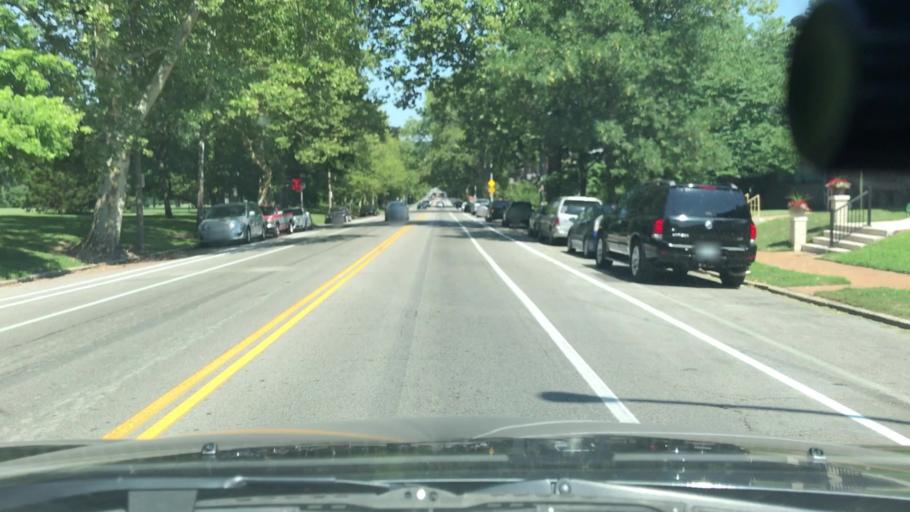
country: US
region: Missouri
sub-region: City of Saint Louis
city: St. Louis
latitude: 38.6043
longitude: -90.2573
